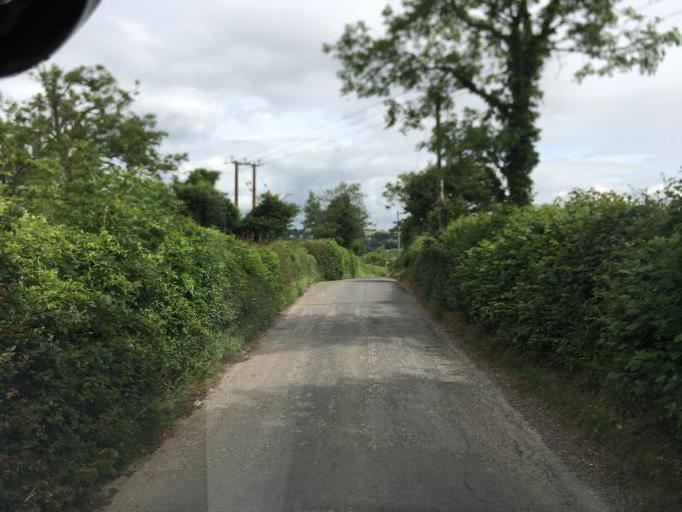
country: GB
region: England
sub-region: Gloucestershire
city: Nailsworth
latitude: 51.6994
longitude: -2.2414
